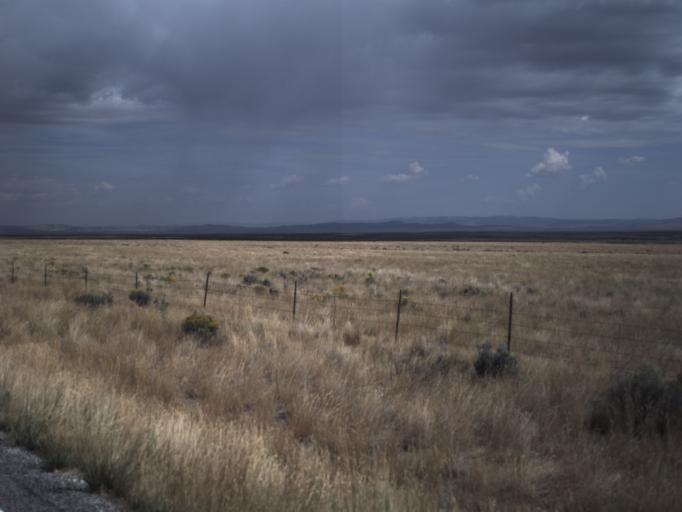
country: US
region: Idaho
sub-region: Oneida County
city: Malad City
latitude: 41.8807
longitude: -113.1175
